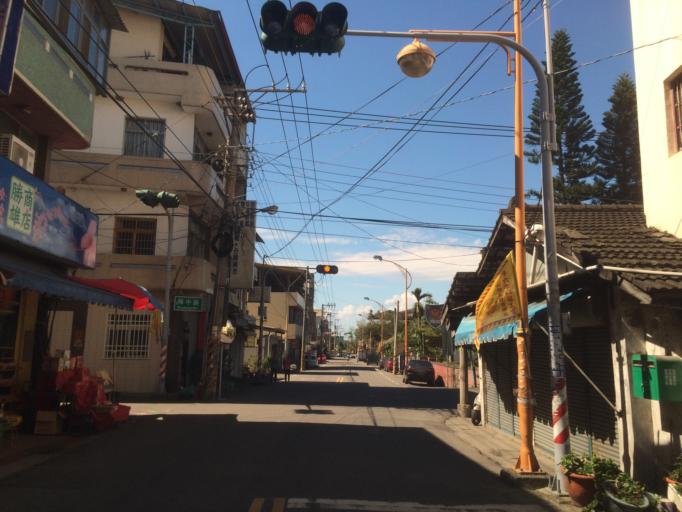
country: TW
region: Taiwan
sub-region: Yunlin
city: Douliu
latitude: 23.7027
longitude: 120.5986
